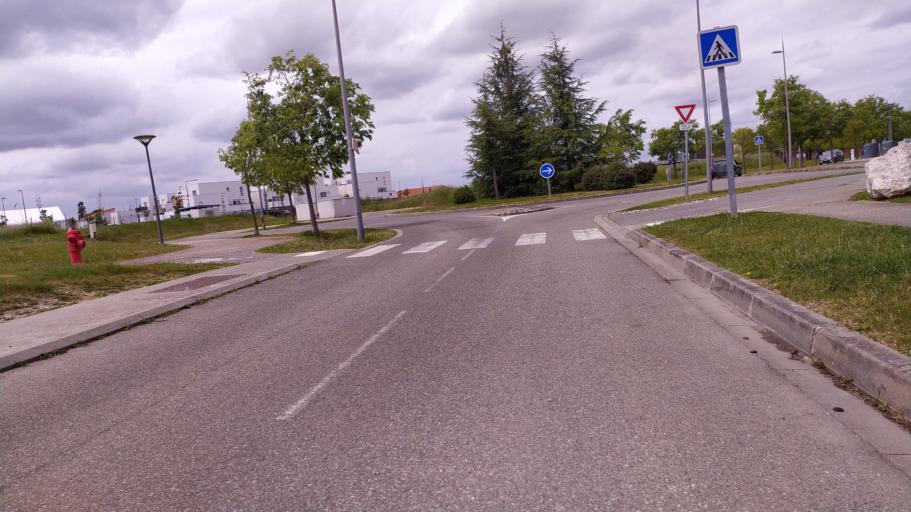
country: FR
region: Midi-Pyrenees
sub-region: Departement de la Haute-Garonne
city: La Salvetat-Saint-Gilles
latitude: 43.5828
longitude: 1.2852
